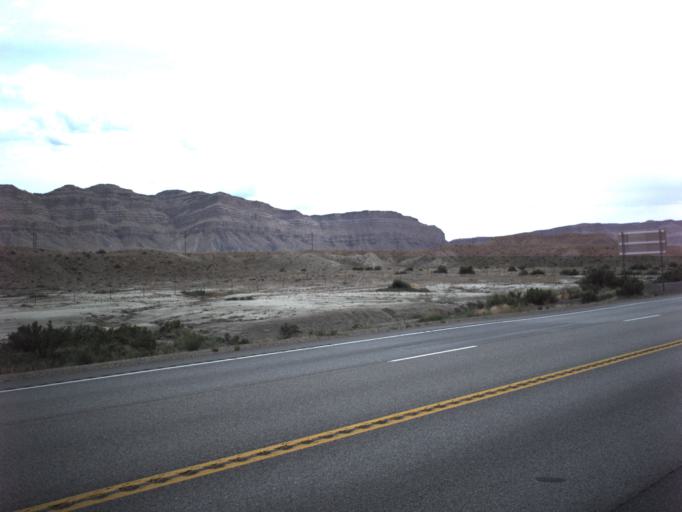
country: US
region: Utah
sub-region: Carbon County
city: East Carbon City
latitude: 39.2951
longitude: -110.3545
